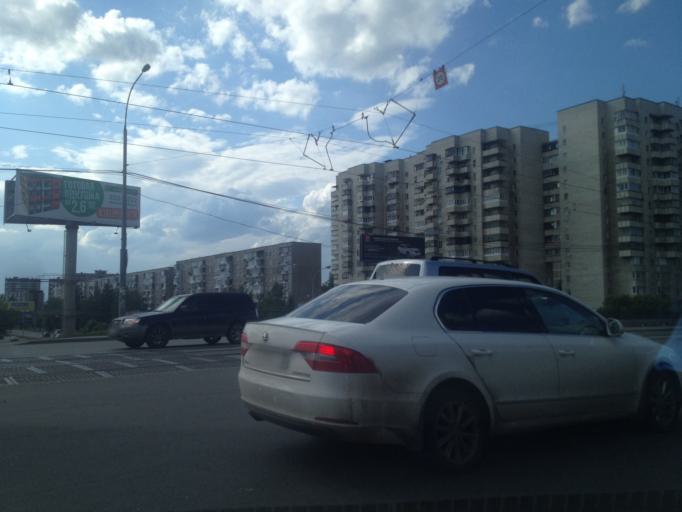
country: RU
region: Sverdlovsk
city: Sovkhoznyy
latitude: 56.8259
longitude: 60.5440
